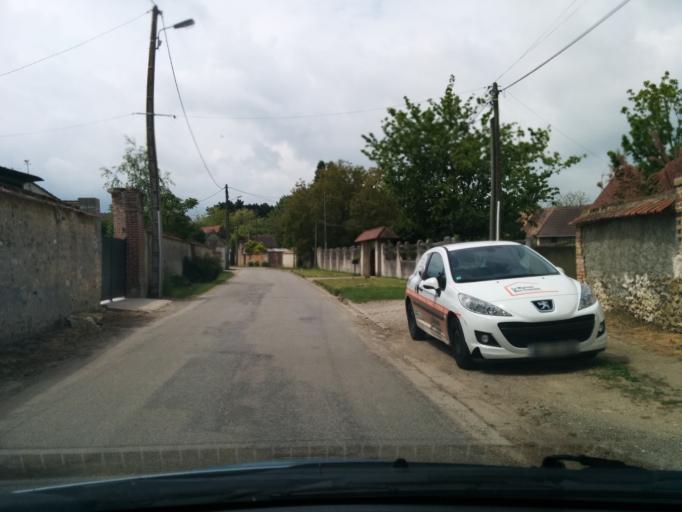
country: FR
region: Haute-Normandie
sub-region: Departement de l'Eure
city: Gasny
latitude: 49.1616
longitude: 1.5501
